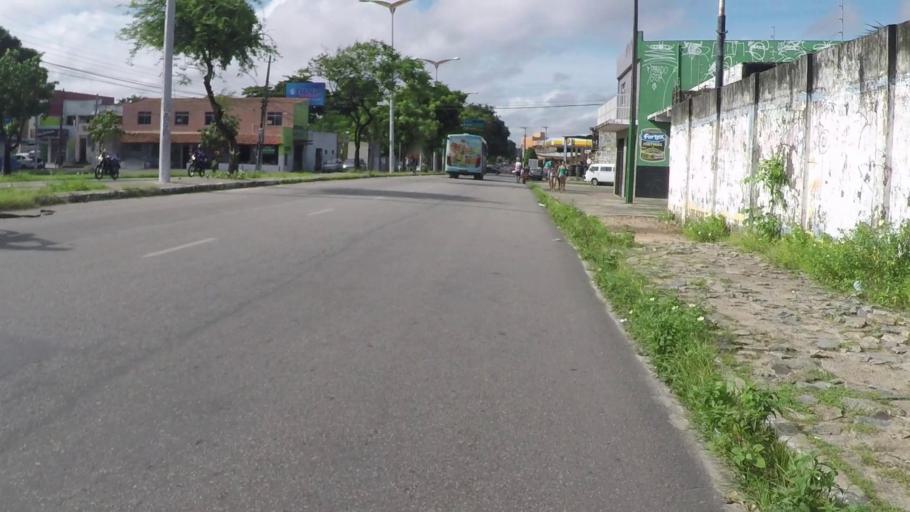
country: BR
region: Ceara
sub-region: Fortaleza
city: Fortaleza
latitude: -3.7092
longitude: -38.5902
